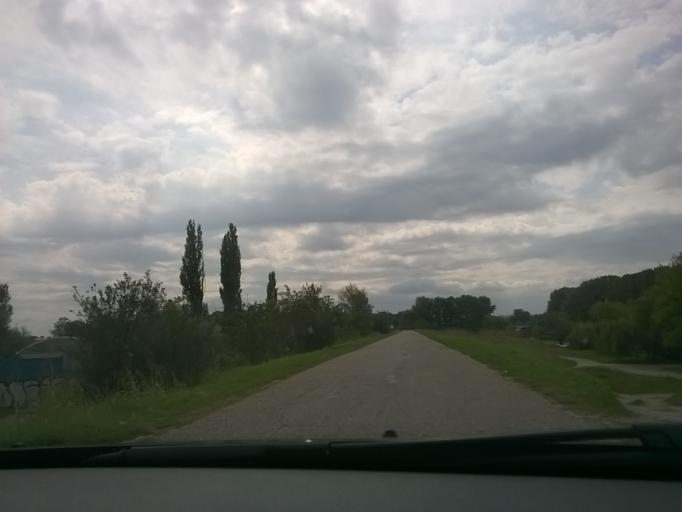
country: RS
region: Autonomna Pokrajina Vojvodina
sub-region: Juznobanatski Okrug
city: Pancevo
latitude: 44.8614
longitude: 20.6391
